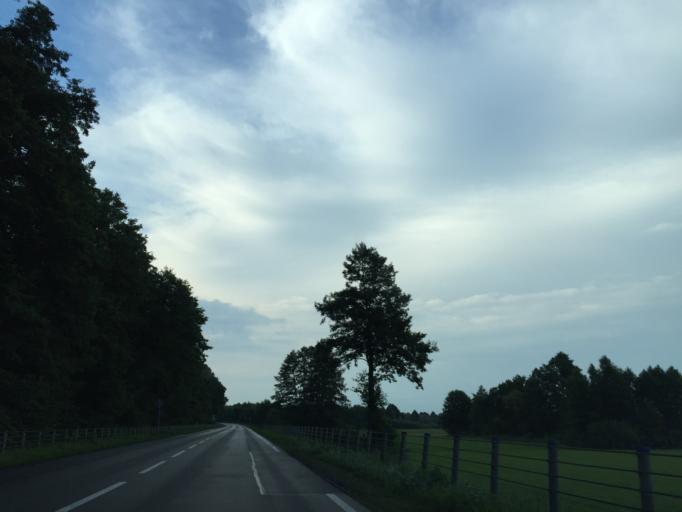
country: PL
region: Masovian Voivodeship
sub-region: Powiat ostrowski
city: Brok
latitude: 52.6866
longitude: 21.8520
